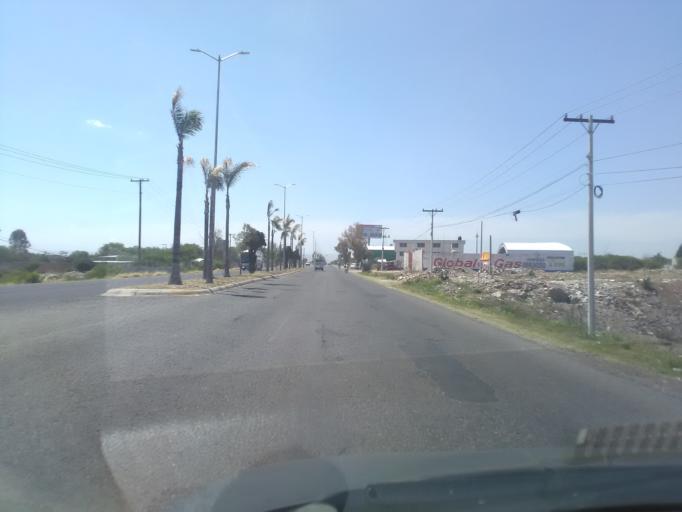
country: MX
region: Durango
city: Victoria de Durango
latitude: 24.0264
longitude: -104.5742
